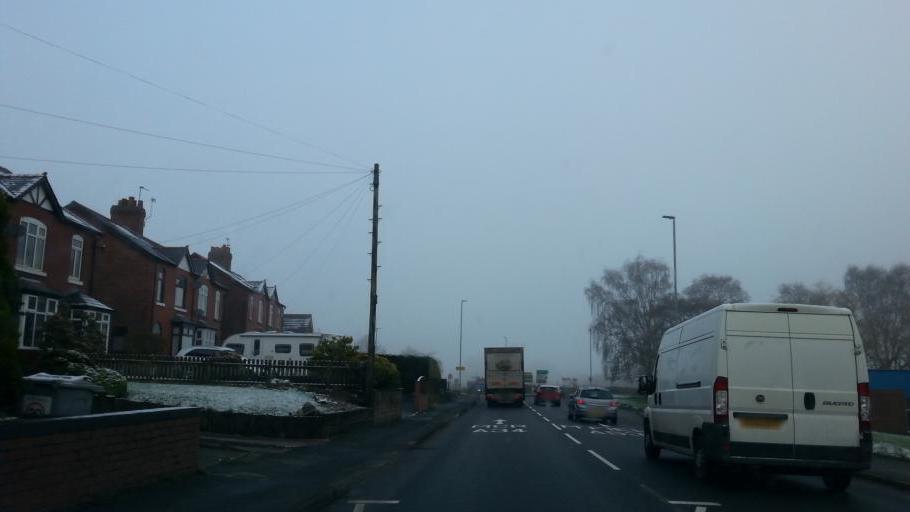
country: GB
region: England
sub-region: Cheshire East
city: Congleton
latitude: 53.1736
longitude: -2.2081
